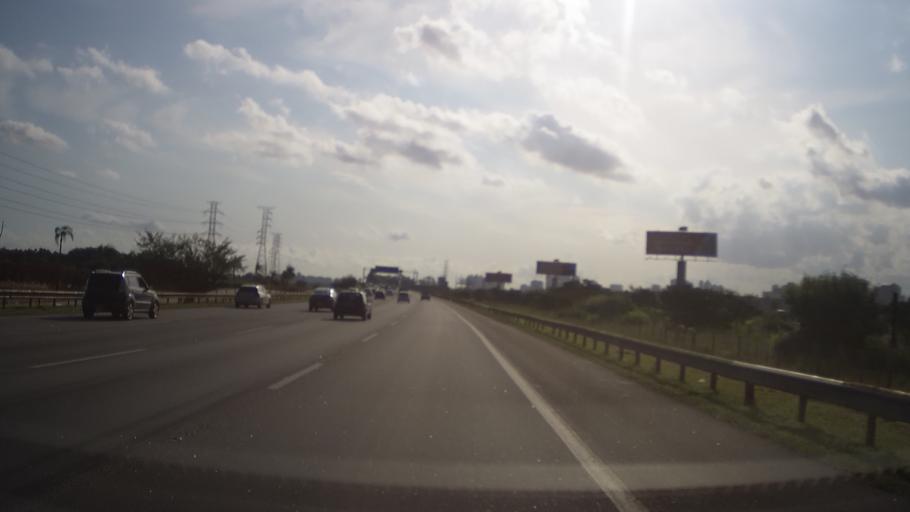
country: BR
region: Sao Paulo
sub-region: Guarulhos
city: Guarulhos
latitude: -23.4737
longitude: -46.5108
